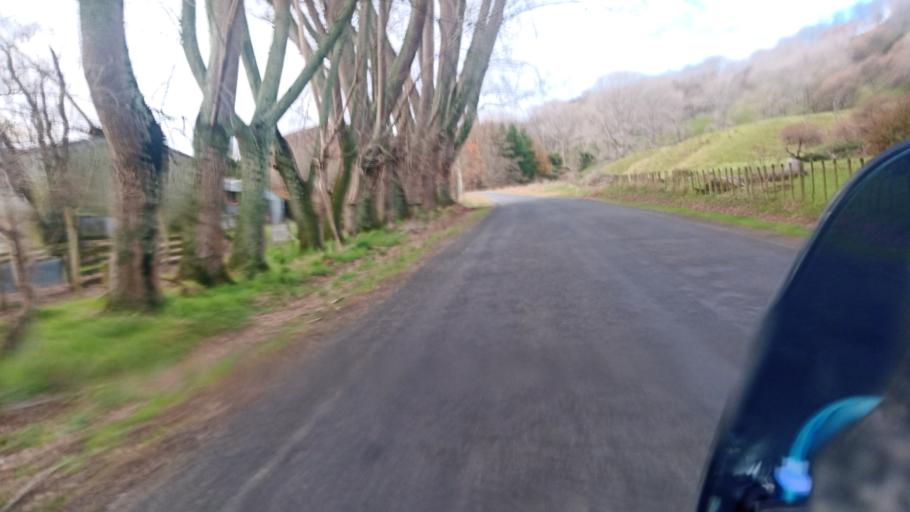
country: NZ
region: Gisborne
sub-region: Gisborne District
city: Gisborne
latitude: -38.4368
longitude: 177.8813
